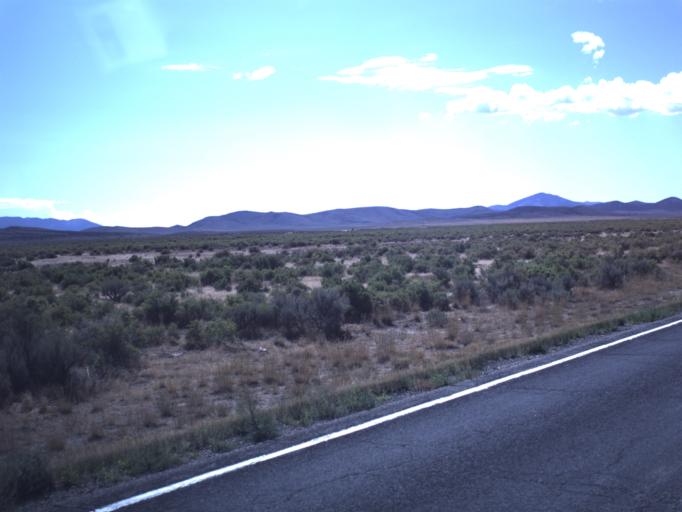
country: US
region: Utah
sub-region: Tooele County
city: Tooele
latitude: 40.1148
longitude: -112.4308
